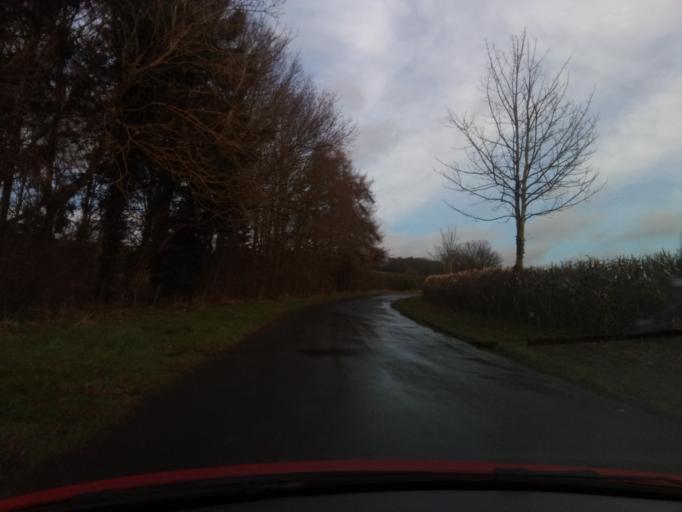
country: GB
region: England
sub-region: Northumberland
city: Corbridge
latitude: 54.9892
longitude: -2.0350
